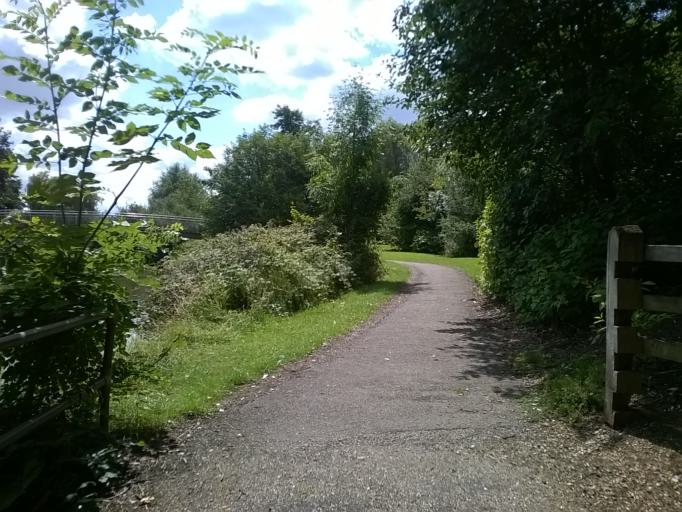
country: GB
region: England
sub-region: Milton Keynes
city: Milton Keynes
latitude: 52.0644
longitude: -0.7450
